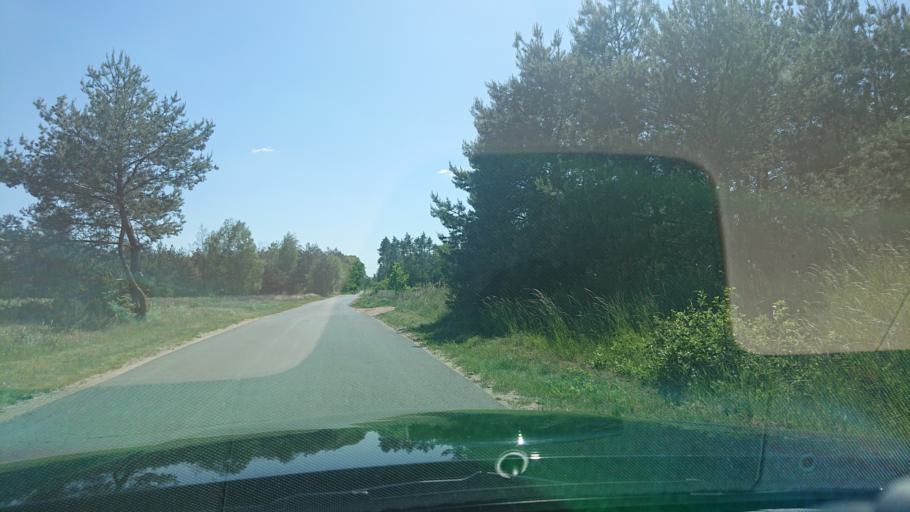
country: PL
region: Greater Poland Voivodeship
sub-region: Powiat gnieznienski
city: Gniezno
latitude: 52.4984
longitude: 17.5825
